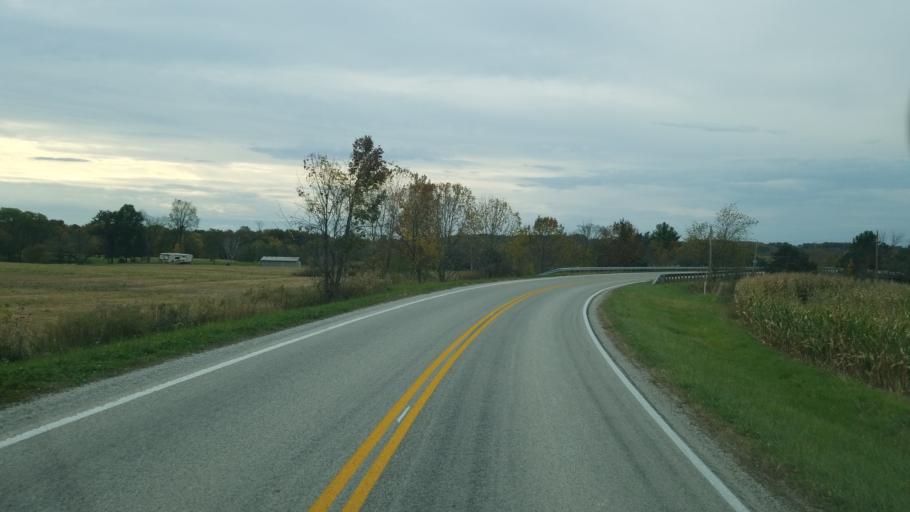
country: US
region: Ohio
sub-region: Ashland County
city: Ashland
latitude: 40.8708
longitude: -82.2221
